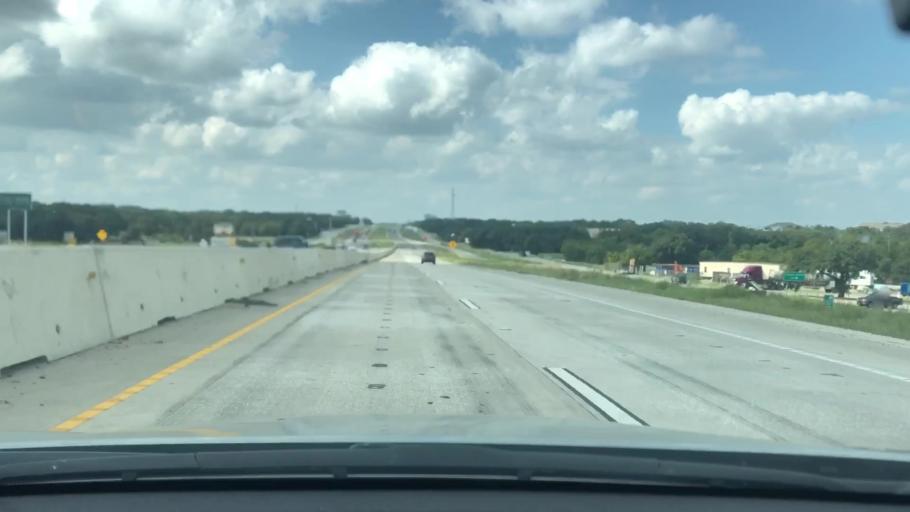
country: US
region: Texas
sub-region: Kendall County
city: Boerne
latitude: 29.7551
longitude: -98.7055
